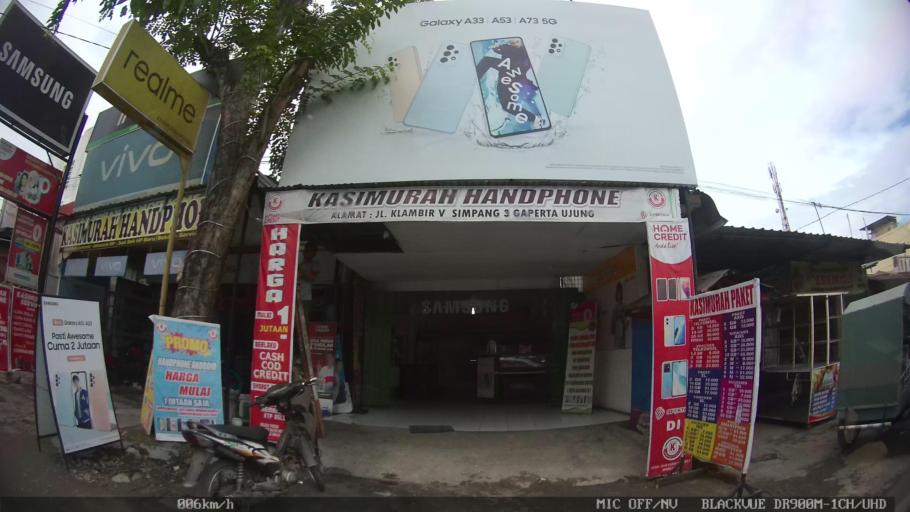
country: ID
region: North Sumatra
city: Sunggal
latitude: 3.6091
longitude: 98.6082
